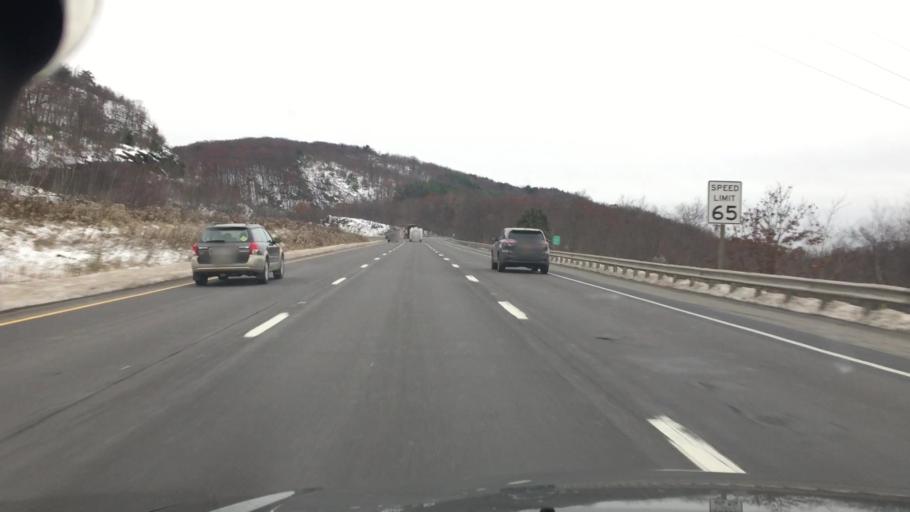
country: US
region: Pennsylvania
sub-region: Luzerne County
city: Ashley
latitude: 41.1964
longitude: -75.9138
